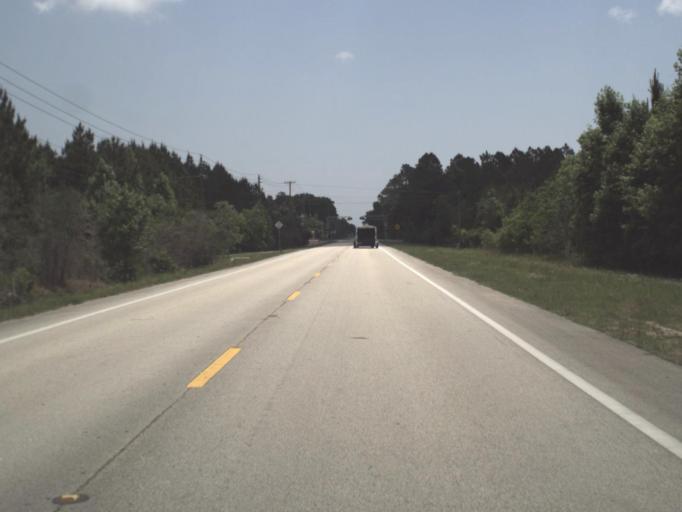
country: US
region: Florida
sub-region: Saint Johns County
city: Saint Augustine Shores
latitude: 29.7563
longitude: -81.3234
